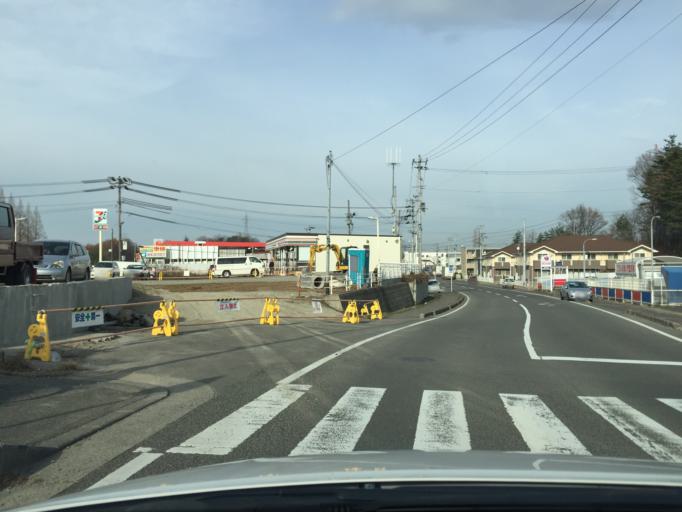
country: JP
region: Fukushima
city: Fukushima-shi
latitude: 37.6947
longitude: 140.4613
